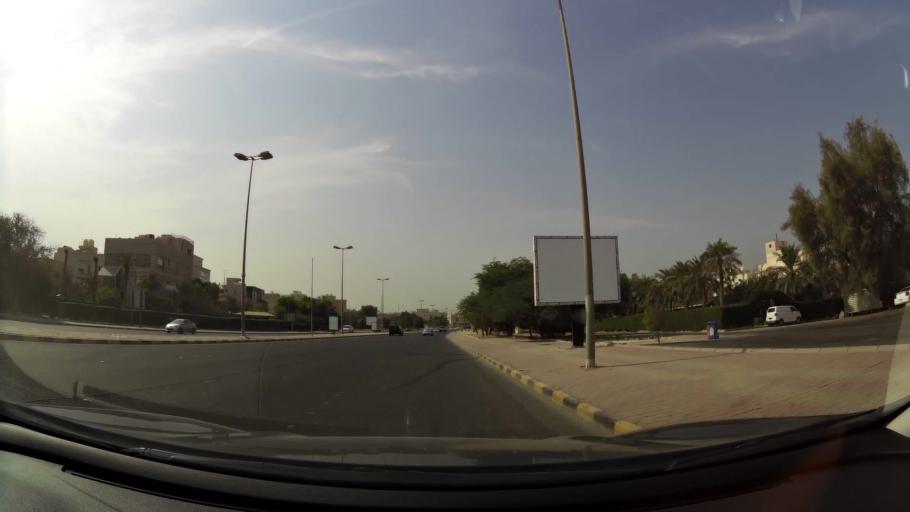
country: KW
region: Al Asimah
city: Ash Shamiyah
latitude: 29.3443
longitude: 47.9669
